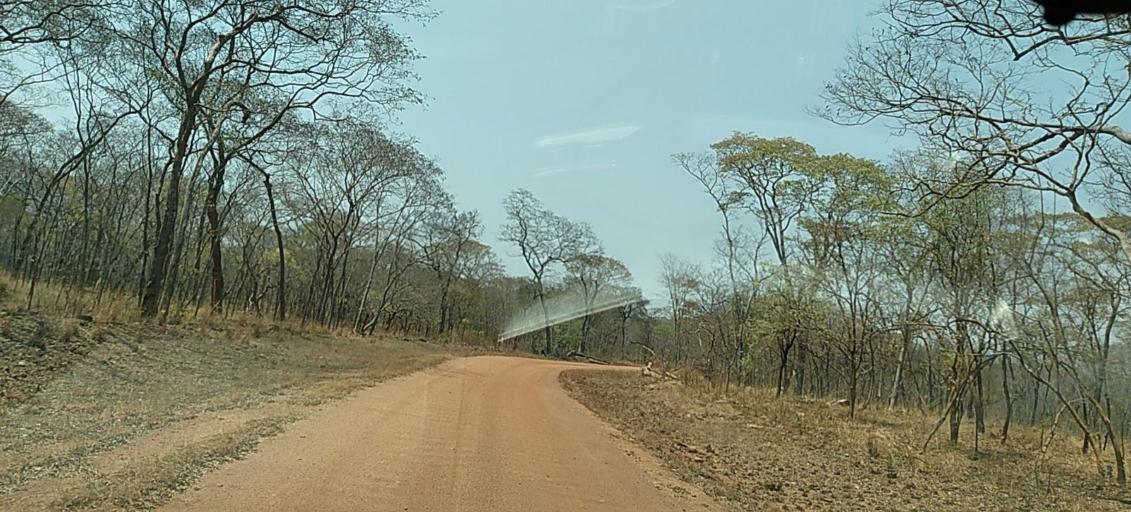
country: ZM
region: Central
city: Mumbwa
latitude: -14.2772
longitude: 26.5247
